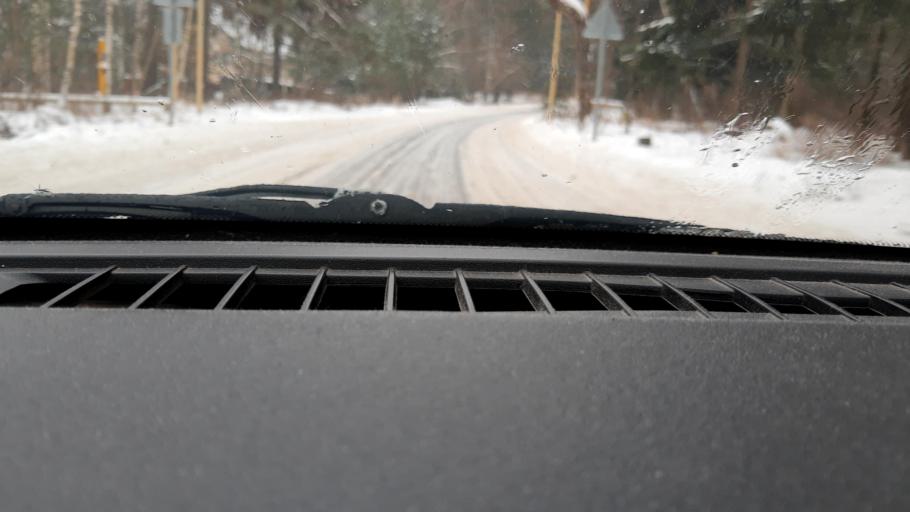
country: RU
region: Nizjnij Novgorod
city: Afonino
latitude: 56.1870
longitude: 44.0790
